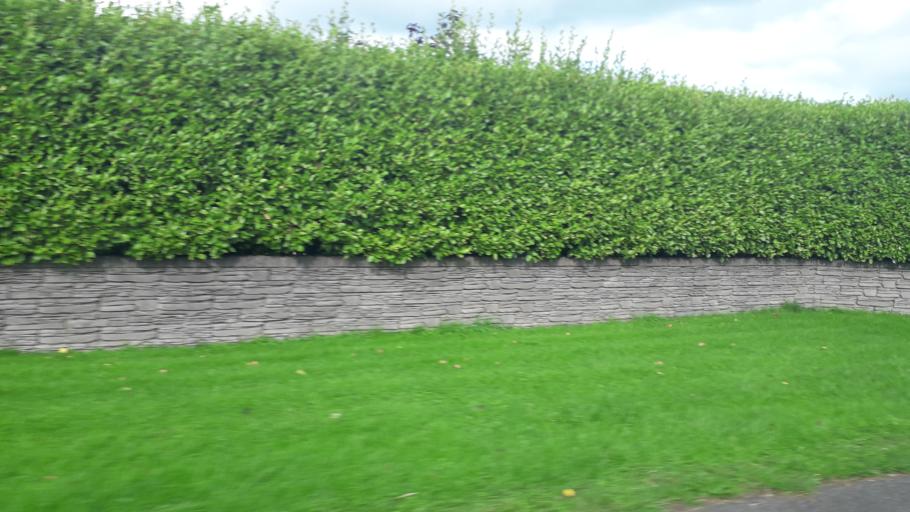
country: IE
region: Leinster
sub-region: Lu
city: Blackrock
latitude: 54.0151
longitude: -6.3189
